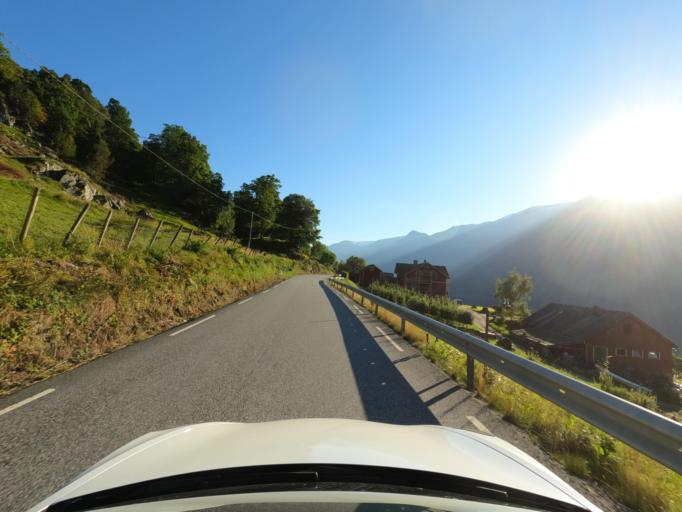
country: NO
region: Hordaland
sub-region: Odda
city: Odda
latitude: 60.2315
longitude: 6.6133
